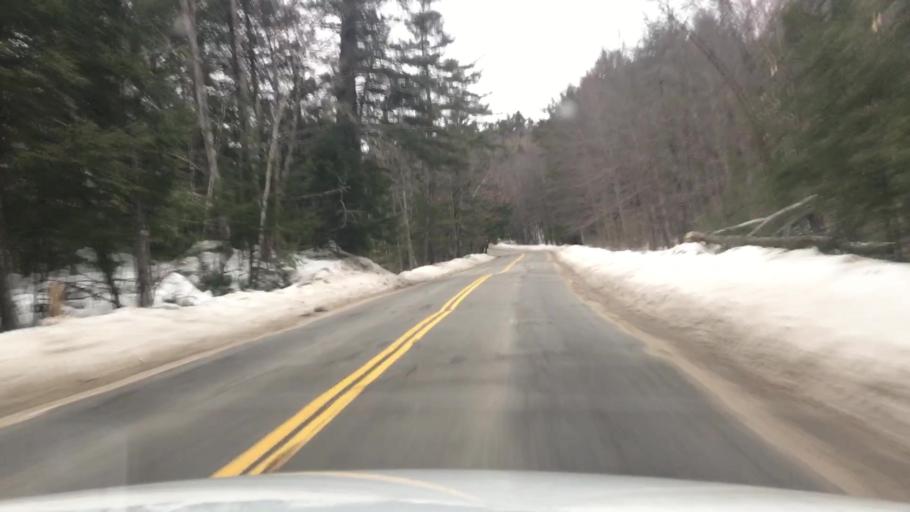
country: US
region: Maine
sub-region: Oxford County
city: Hiram
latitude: 43.8947
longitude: -70.7913
